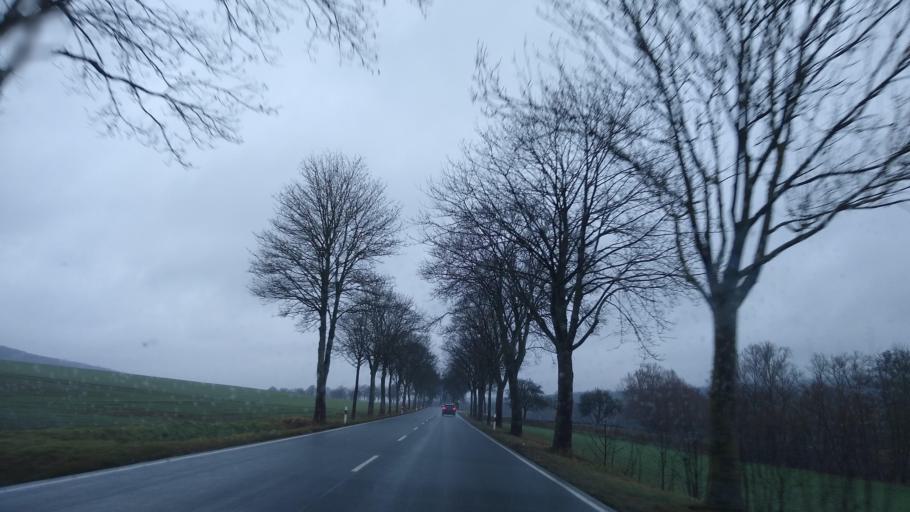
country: DE
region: Lower Saxony
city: Eimen
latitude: 51.8730
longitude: 9.8013
